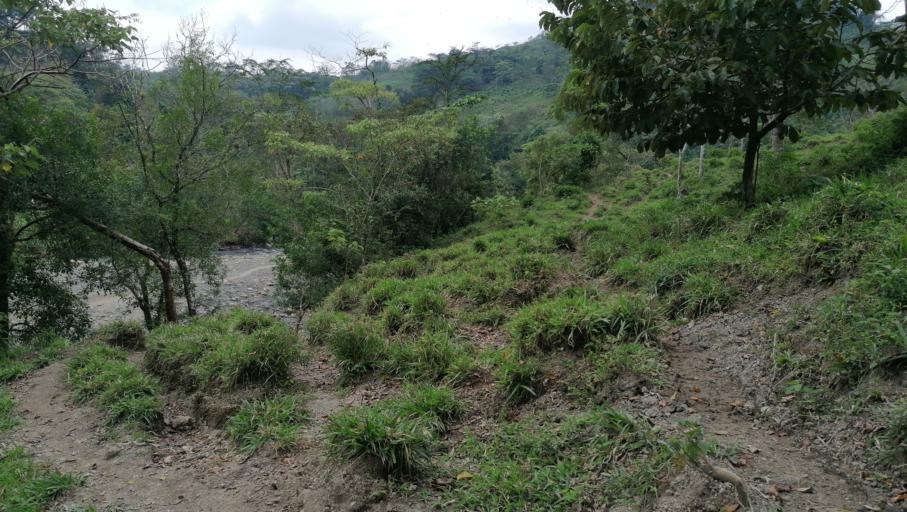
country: MX
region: Chiapas
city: Ocotepec
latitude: 17.2981
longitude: -93.2276
